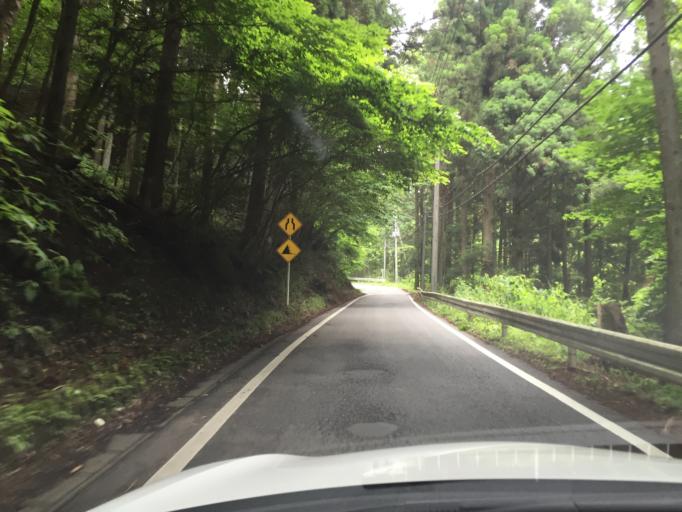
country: JP
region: Fukushima
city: Iwaki
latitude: 37.1434
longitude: 140.7008
